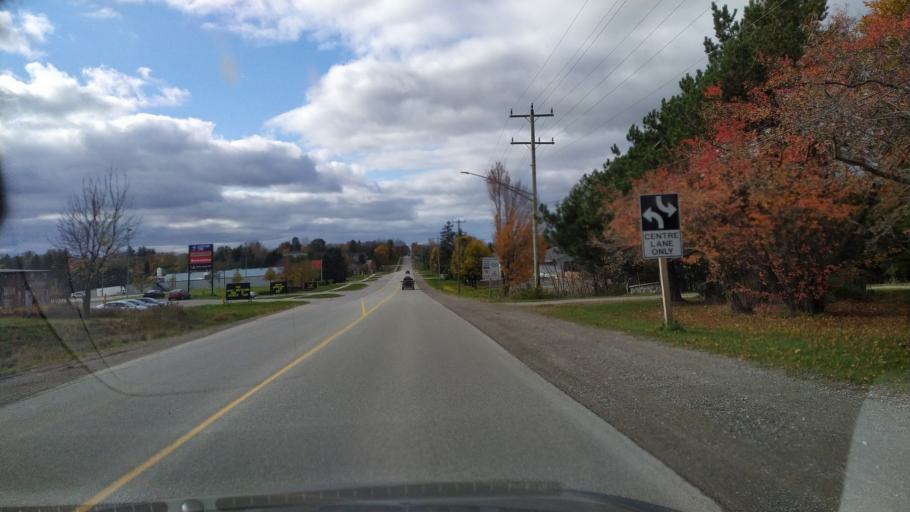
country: CA
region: Ontario
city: Stratford
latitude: 43.2626
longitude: -81.1141
